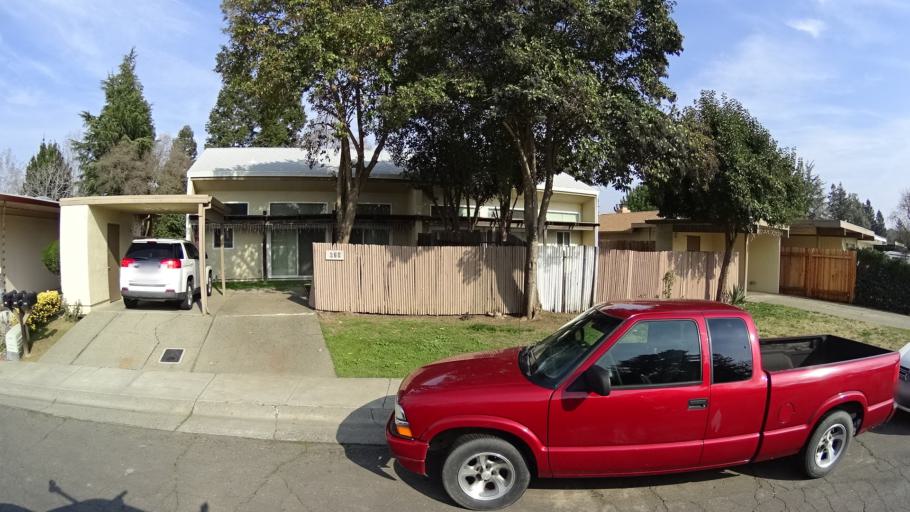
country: US
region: California
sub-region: Yolo County
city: Davis
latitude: 38.5696
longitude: -121.7580
